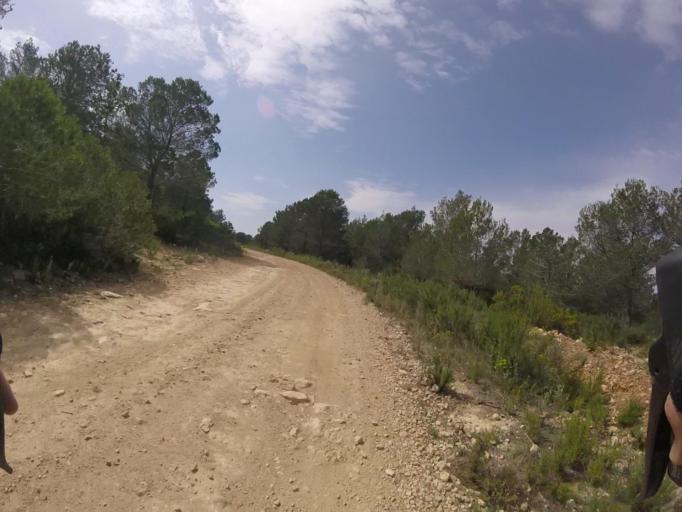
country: ES
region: Valencia
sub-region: Provincia de Castello
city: Cuevas de Vinroma
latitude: 40.2798
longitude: 0.1228
